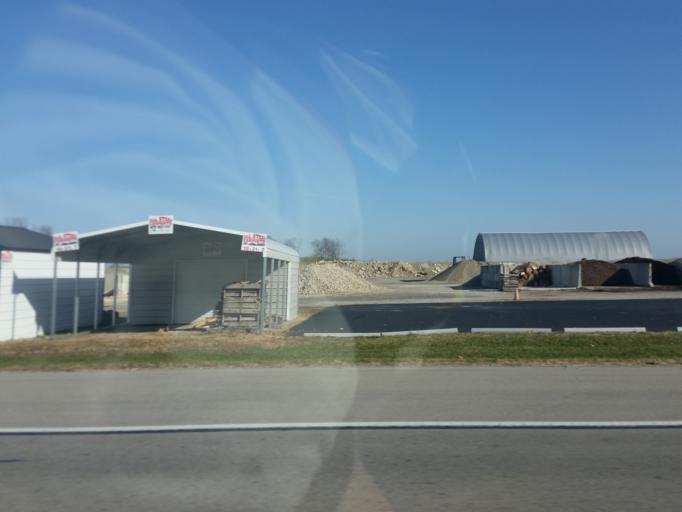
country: US
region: Ohio
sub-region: Butler County
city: Oxford
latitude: 39.4371
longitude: -84.6800
